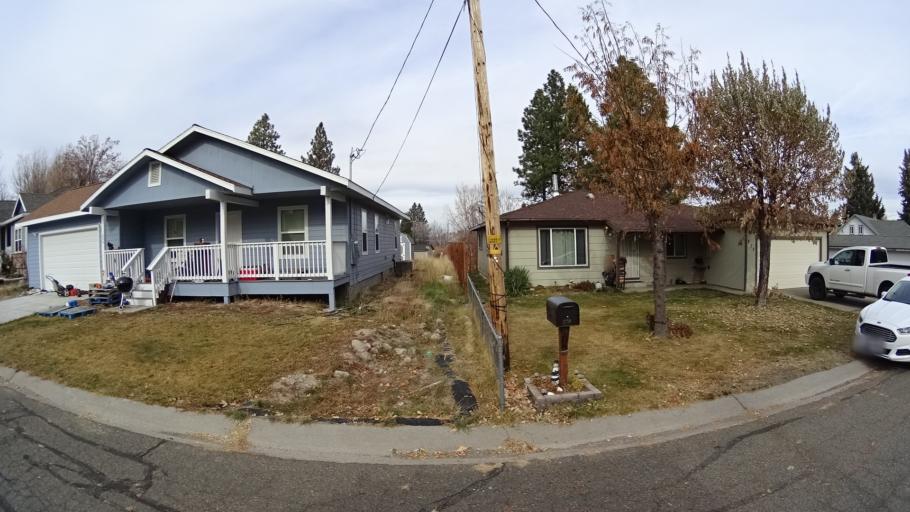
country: US
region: California
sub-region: Siskiyou County
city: Weed
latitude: 41.4277
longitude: -122.3755
